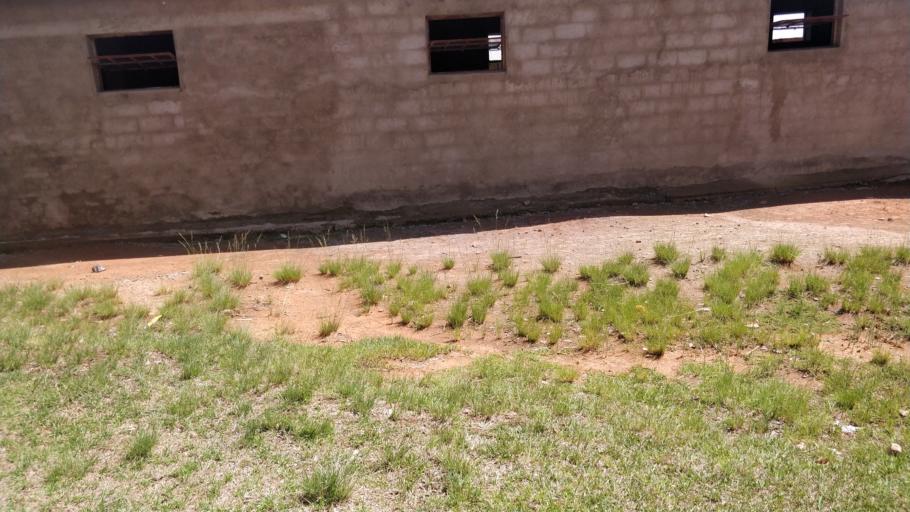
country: LS
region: Maseru
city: Nako
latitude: -29.6299
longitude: 27.5056
